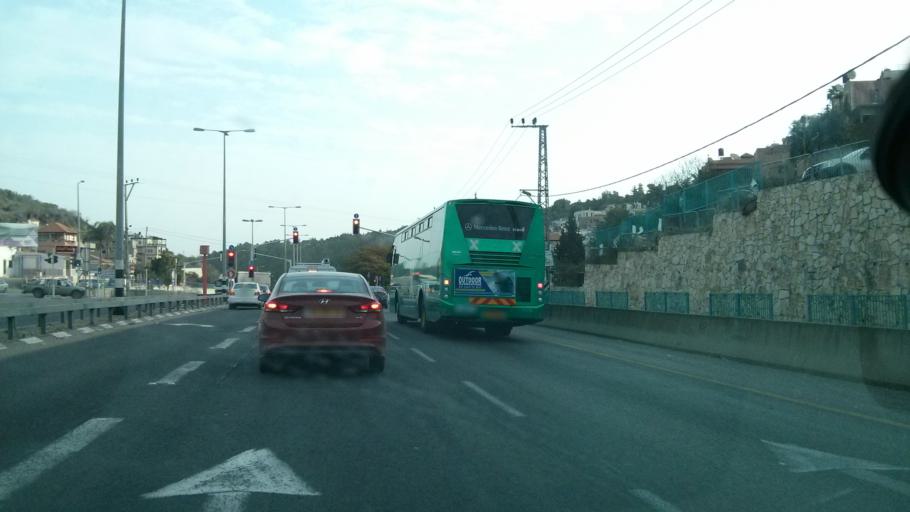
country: IL
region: Haifa
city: Umm el Fahm
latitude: 32.5413
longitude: 35.1561
